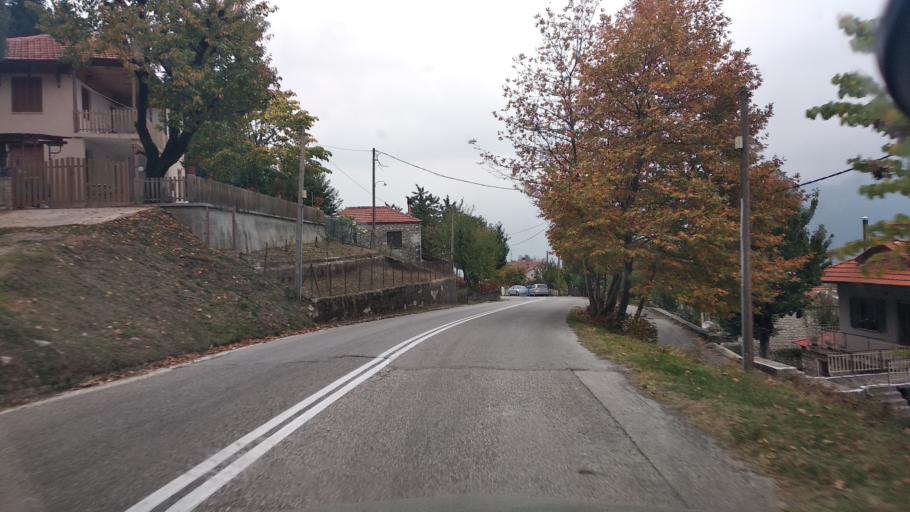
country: GR
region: Thessaly
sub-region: Trikala
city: Pyli
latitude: 39.5059
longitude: 21.5350
